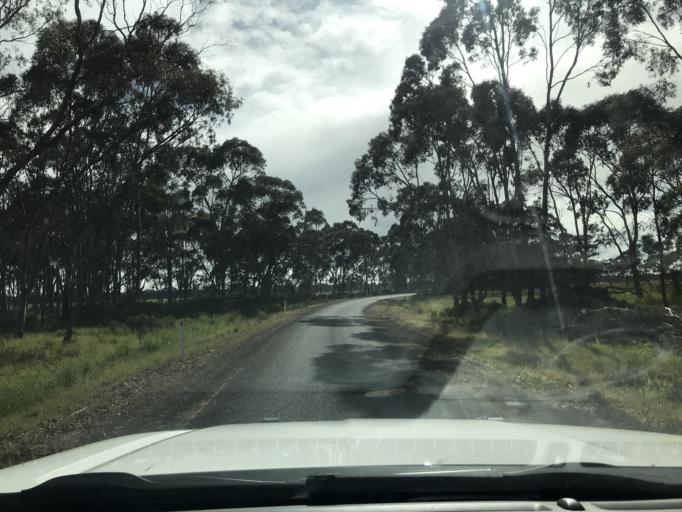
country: AU
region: South Australia
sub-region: Wattle Range
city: Penola
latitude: -37.1851
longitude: 141.2003
